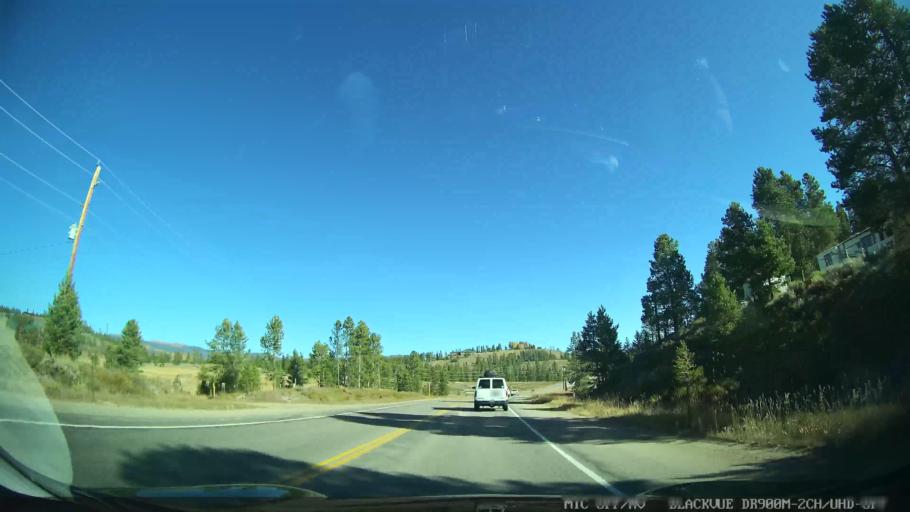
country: US
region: Colorado
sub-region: Grand County
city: Granby
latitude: 40.1723
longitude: -105.9008
